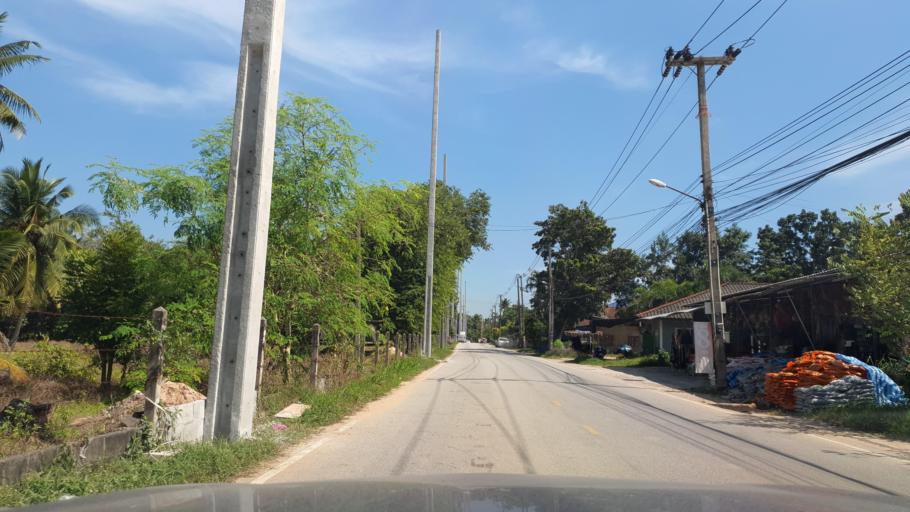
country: TH
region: Chon Buri
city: Bang Lamung
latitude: 12.9807
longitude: 100.9617
